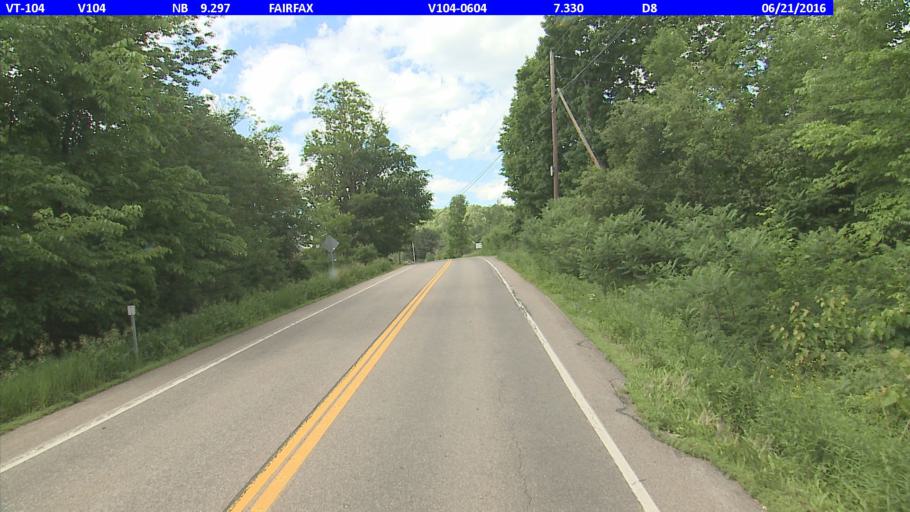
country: US
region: Vermont
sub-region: Chittenden County
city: Milton
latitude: 44.6906
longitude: -73.0333
